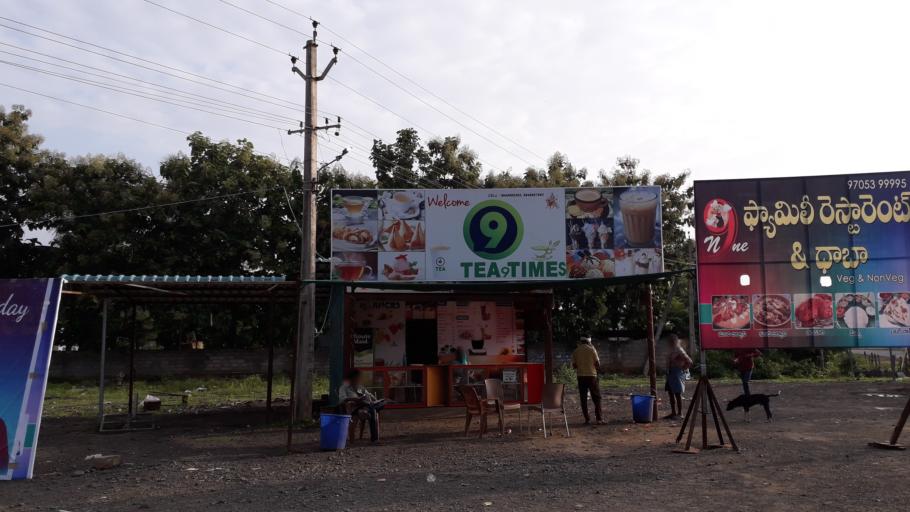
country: IN
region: Andhra Pradesh
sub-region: East Godavari
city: Rajahmundry
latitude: 17.0414
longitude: 81.8386
